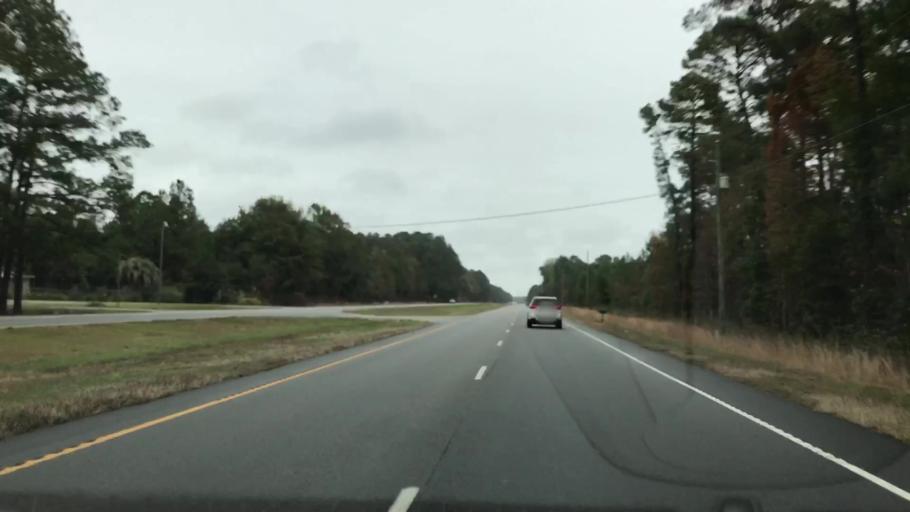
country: US
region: South Carolina
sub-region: Charleston County
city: Awendaw
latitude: 33.1042
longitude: -79.4651
